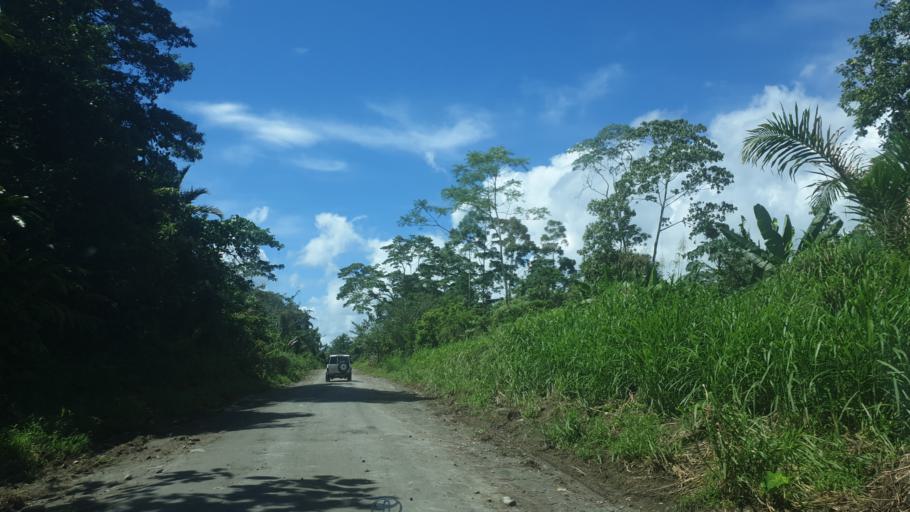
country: PG
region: Bougainville
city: Panguna
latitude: -6.6611
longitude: 155.4511
